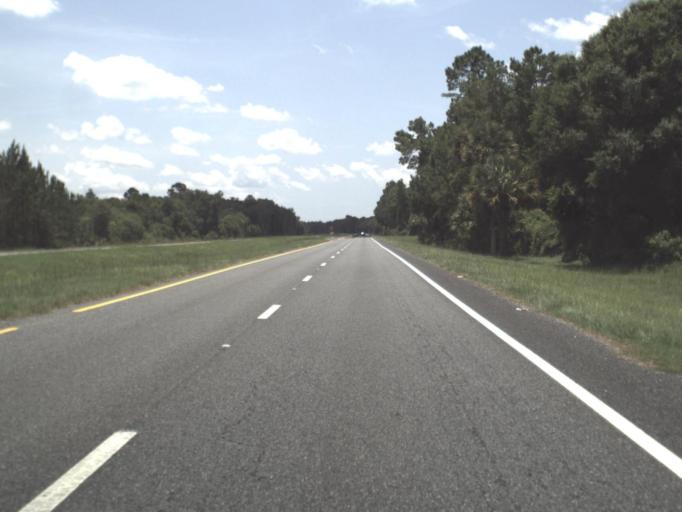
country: US
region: Florida
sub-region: Taylor County
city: Steinhatchee
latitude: 29.7578
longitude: -83.3222
